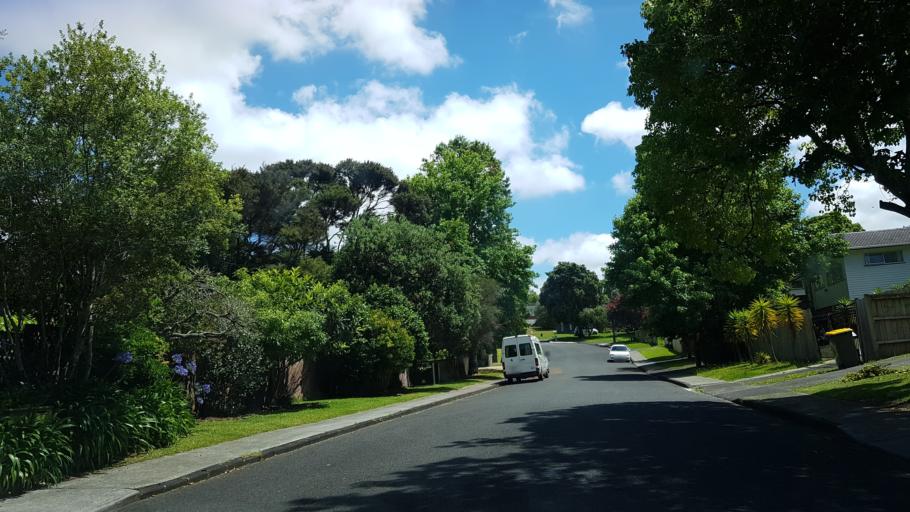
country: NZ
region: Auckland
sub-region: Auckland
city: North Shore
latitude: -36.7772
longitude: 174.7162
